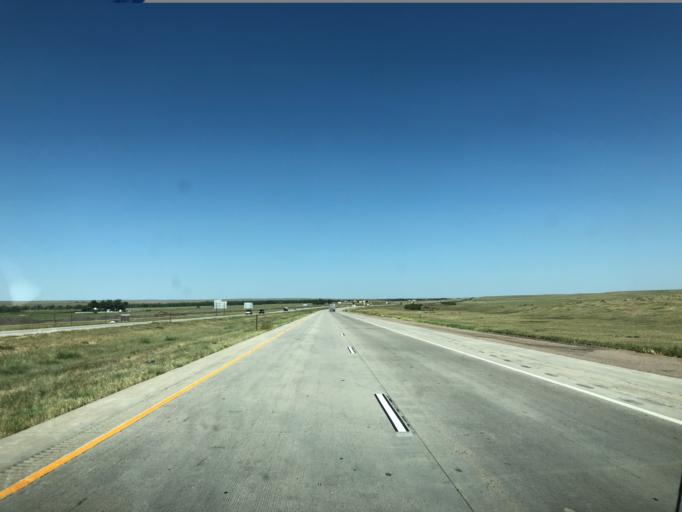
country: US
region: Colorado
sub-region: Lincoln County
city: Limon
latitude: 39.2734
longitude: -103.7272
